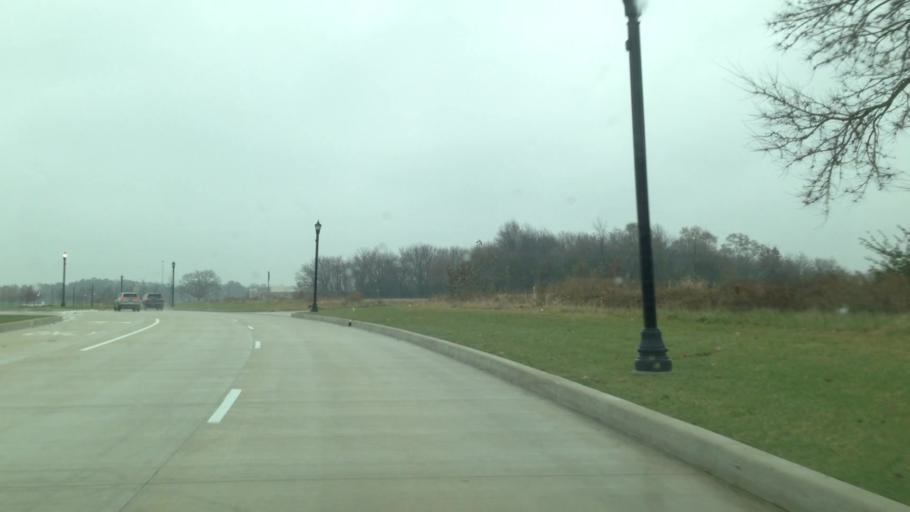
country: US
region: Indiana
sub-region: Saint Joseph County
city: Granger
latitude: 41.7280
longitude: -86.1523
